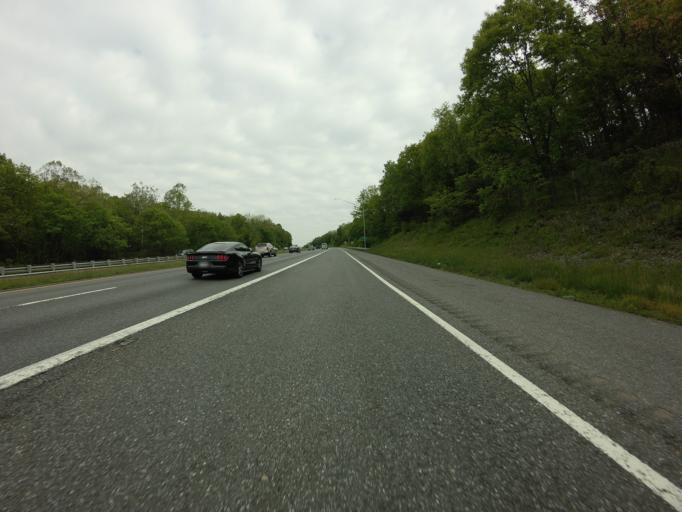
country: US
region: Maryland
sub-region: Frederick County
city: Green Valley
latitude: 39.2796
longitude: -77.3240
